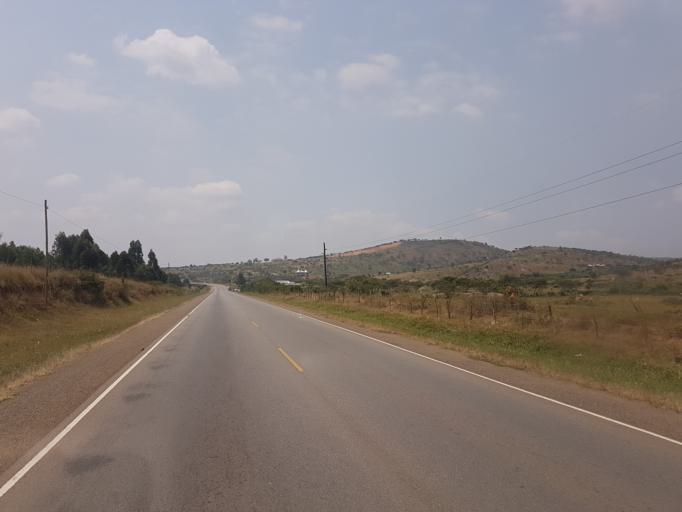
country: UG
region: Western Region
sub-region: Mbarara District
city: Mbarara
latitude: -0.5045
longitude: 30.8468
